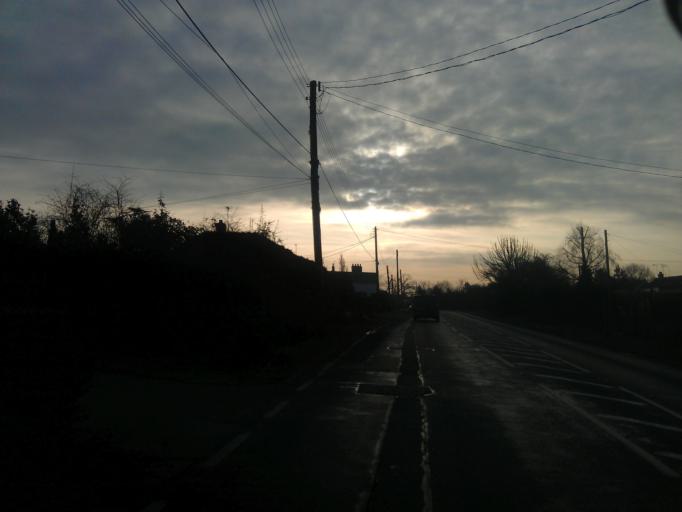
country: GB
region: England
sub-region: Essex
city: Alresford
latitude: 51.8577
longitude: 0.9994
